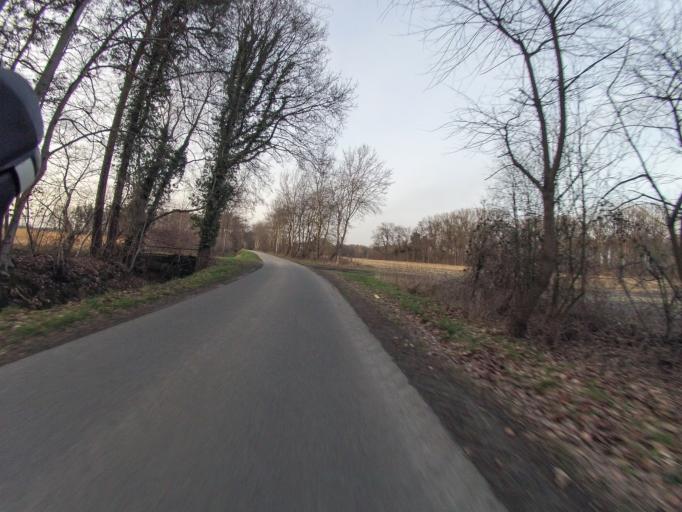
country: DE
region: North Rhine-Westphalia
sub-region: Regierungsbezirk Munster
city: Wettringen
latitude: 52.1822
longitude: 7.3320
